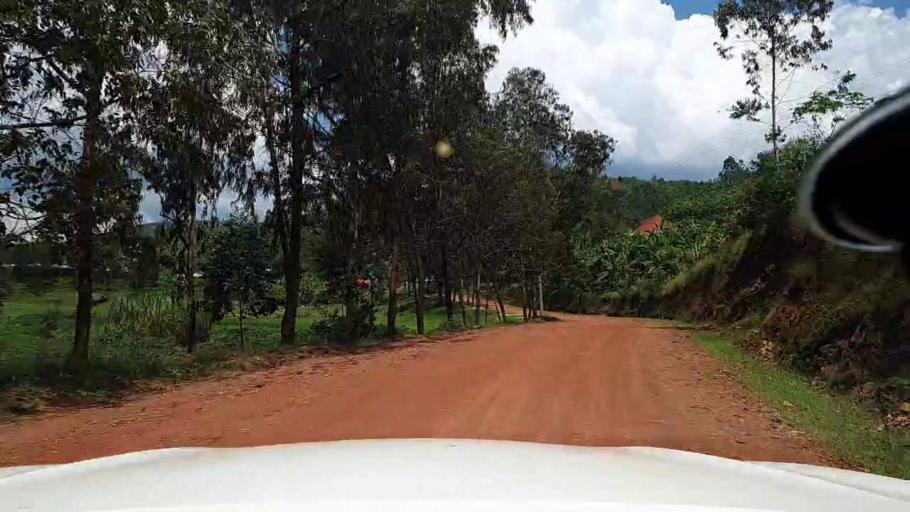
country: RW
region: Northern Province
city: Byumba
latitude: -1.6995
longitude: 29.8308
